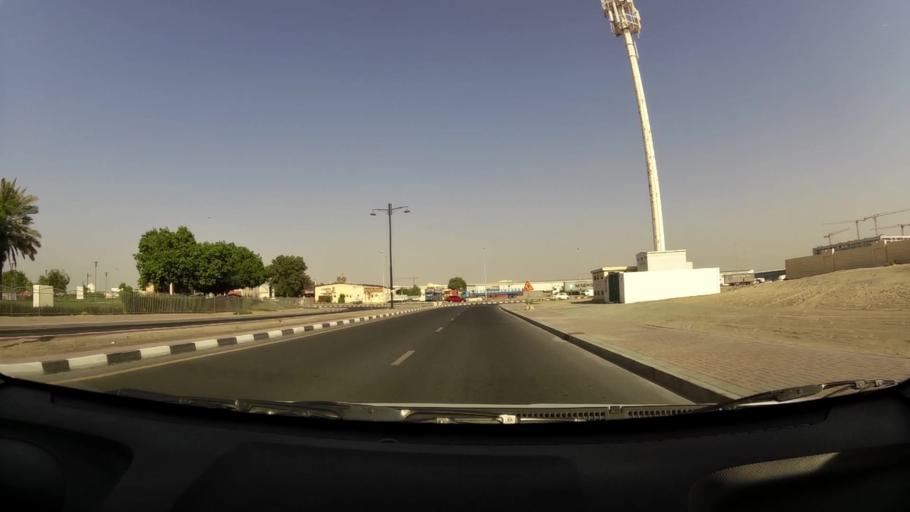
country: AE
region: Ash Shariqah
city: Sharjah
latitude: 25.2861
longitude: 55.3804
